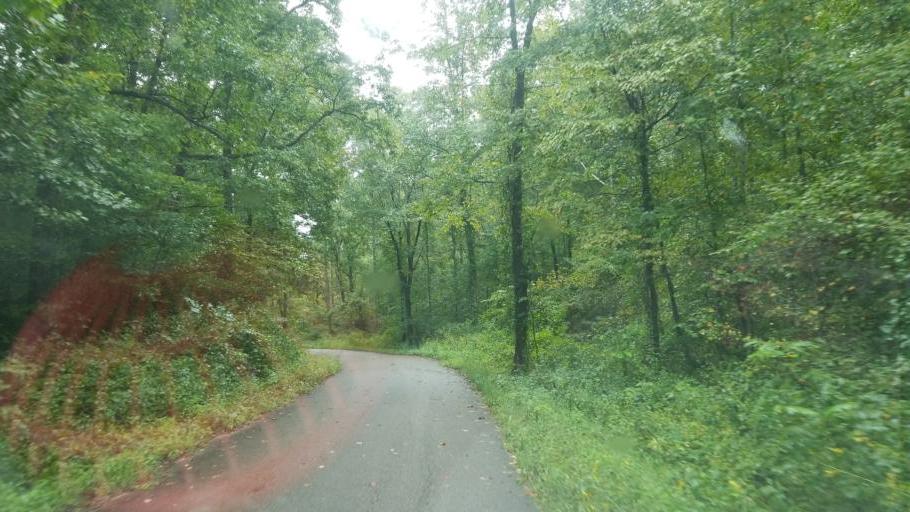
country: US
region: Ohio
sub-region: Scioto County
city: West Portsmouth
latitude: 38.7731
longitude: -83.1399
